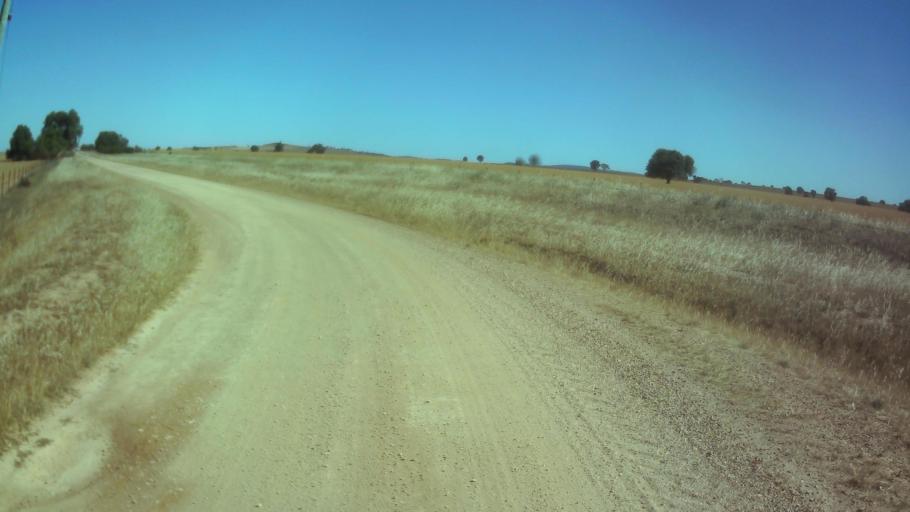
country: AU
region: New South Wales
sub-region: Weddin
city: Grenfell
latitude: -33.9895
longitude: 148.3376
